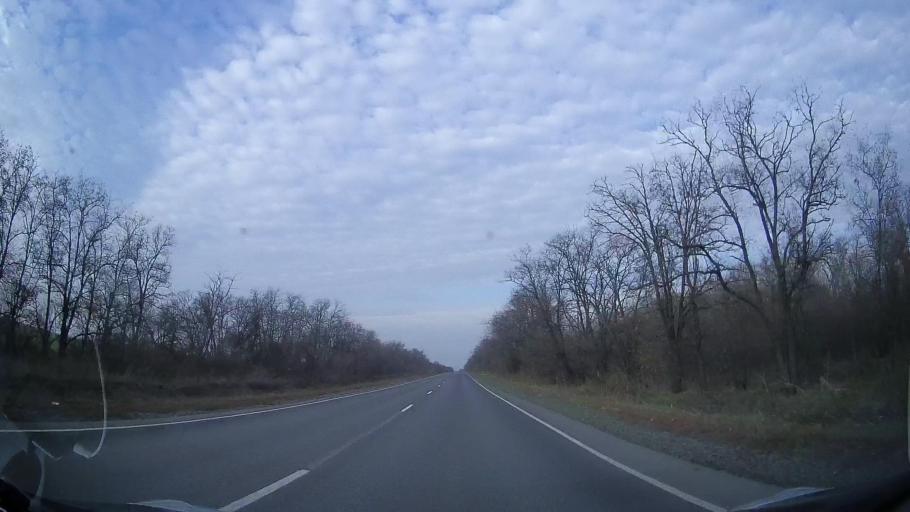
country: RU
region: Rostov
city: Bagayevskaya
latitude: 47.1236
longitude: 40.2767
